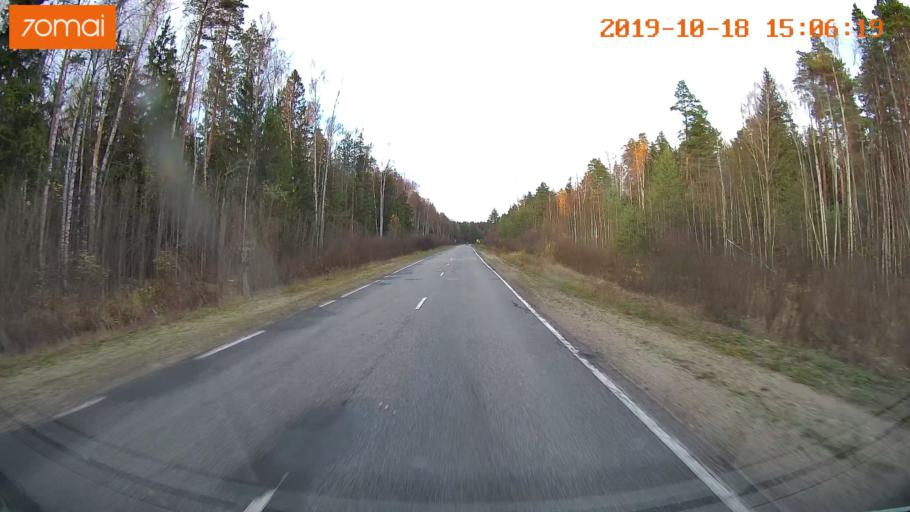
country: RU
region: Vladimir
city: Gus'-Khrustal'nyy
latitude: 55.5284
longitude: 40.5778
